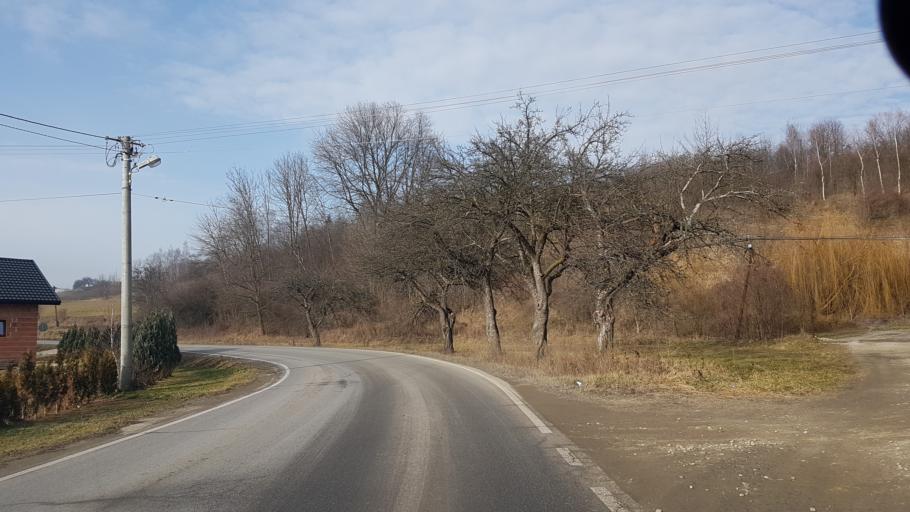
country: PL
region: Lesser Poland Voivodeship
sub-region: Powiat nowosadecki
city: Podegrodzie
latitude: 49.5610
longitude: 20.5728
